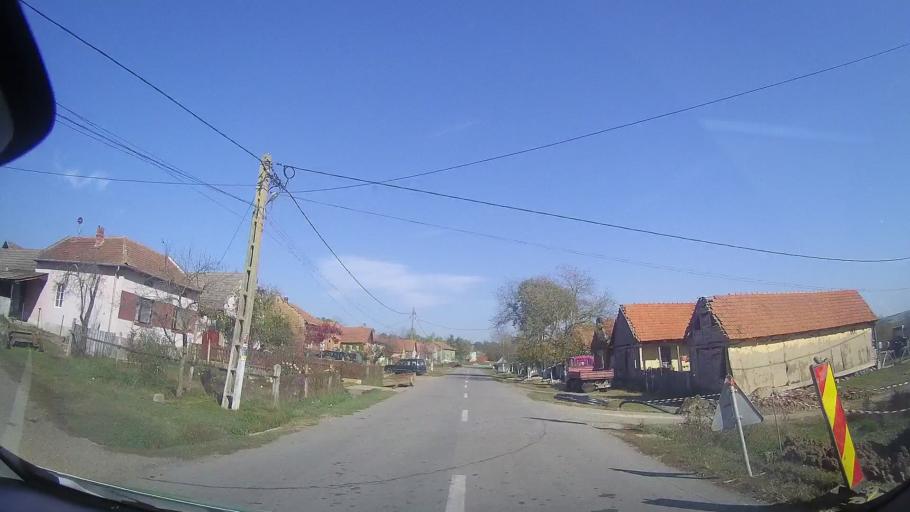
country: RO
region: Timis
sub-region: Comuna Secas
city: Secas
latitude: 45.8496
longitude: 21.7934
